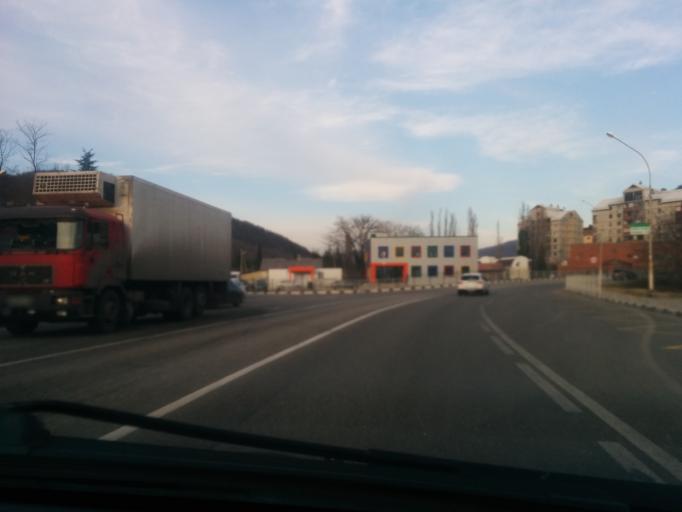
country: RU
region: Krasnodarskiy
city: Agoy
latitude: 44.1464
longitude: 39.0389
